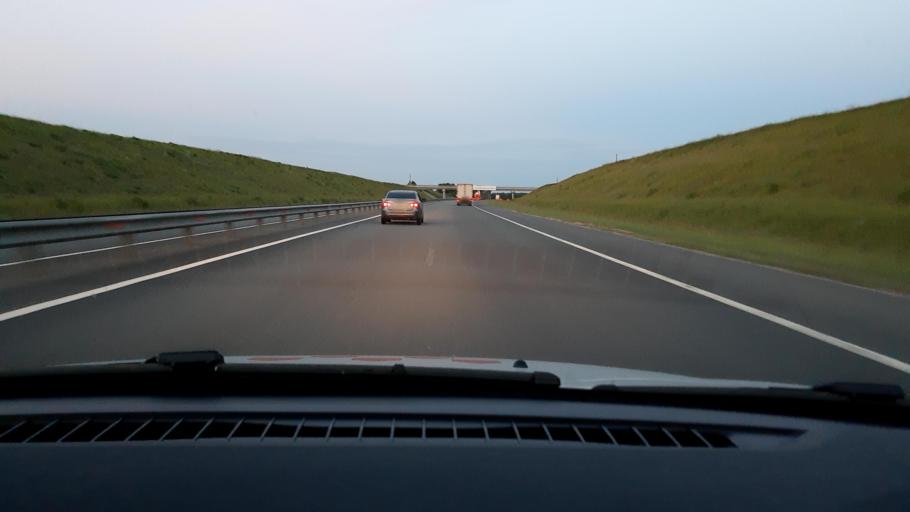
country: RU
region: Nizjnij Novgorod
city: Kstovo
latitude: 56.0950
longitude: 44.0737
